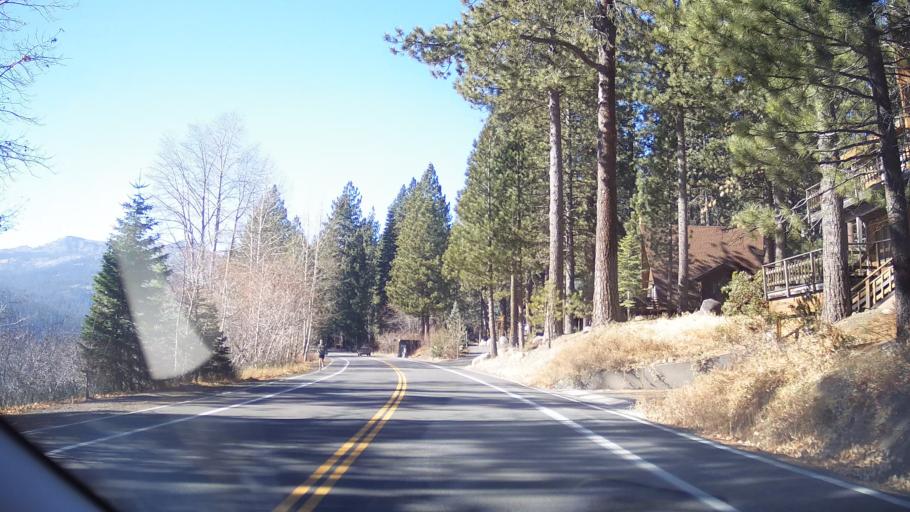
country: US
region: California
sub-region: Nevada County
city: Truckee
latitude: 39.3292
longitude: -120.2563
